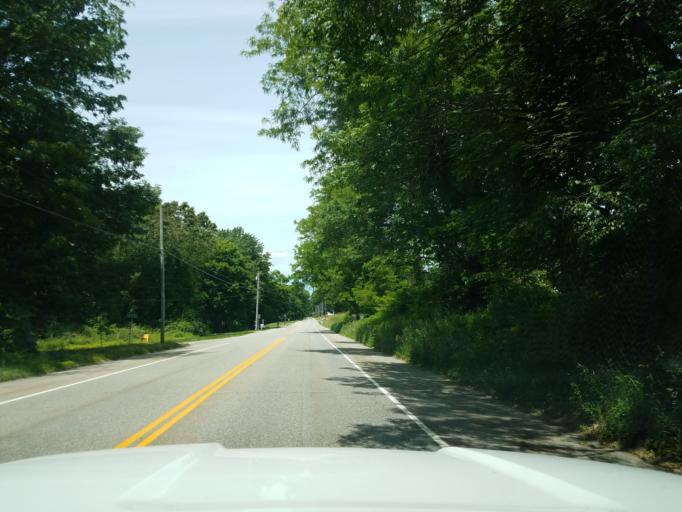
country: US
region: Connecticut
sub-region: New London County
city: Baltic
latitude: 41.5936
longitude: -72.1619
